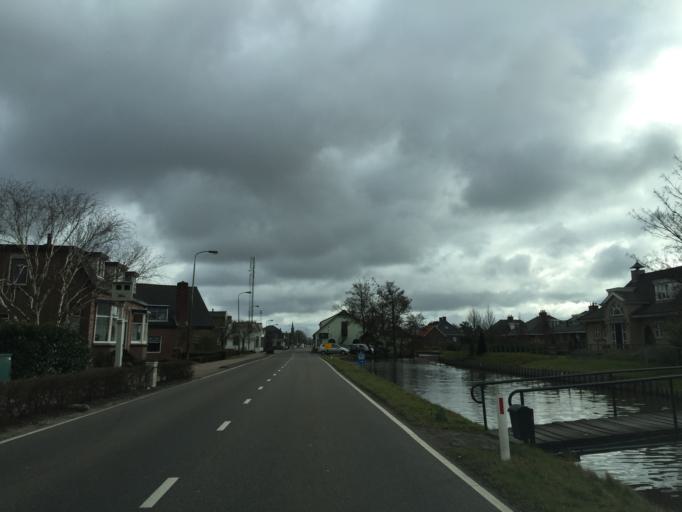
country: NL
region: South Holland
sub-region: Gemeente Lansingerland
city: Berkel en Rodenrijs
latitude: 52.0092
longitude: 4.4842
